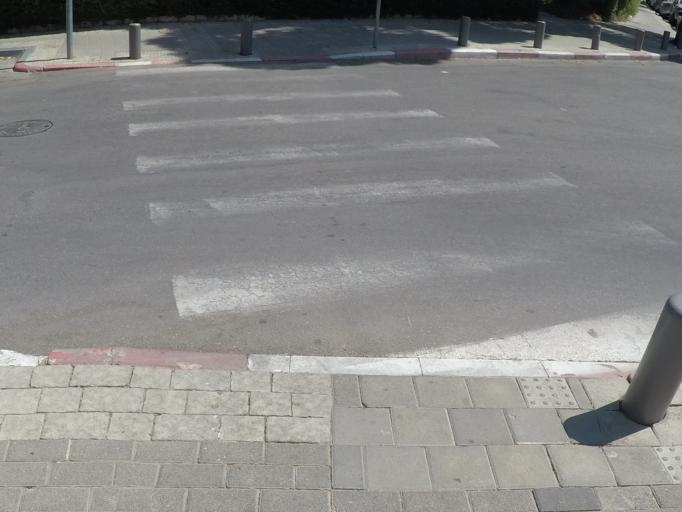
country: IL
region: Tel Aviv
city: Ramat Gan
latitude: 32.1057
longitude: 34.7982
